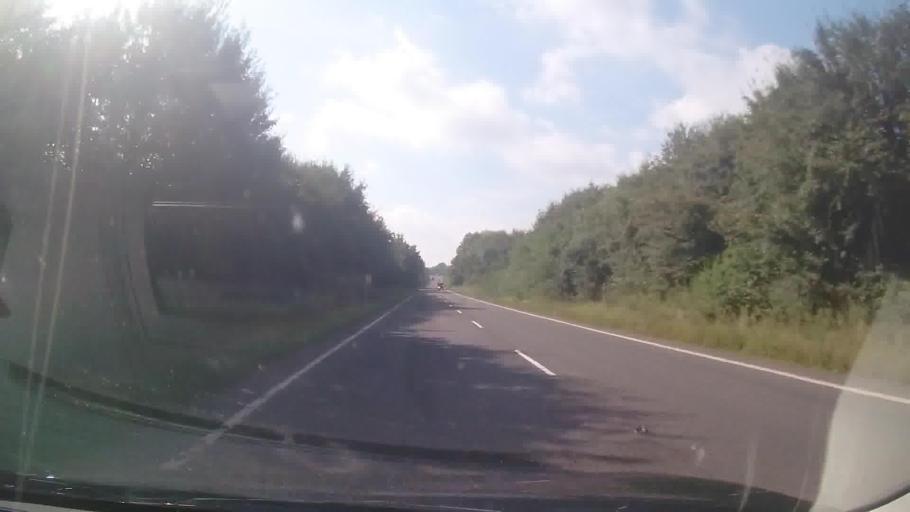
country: GB
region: England
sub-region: Shropshire
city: Whitchurch
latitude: 52.9810
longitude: -2.6971
